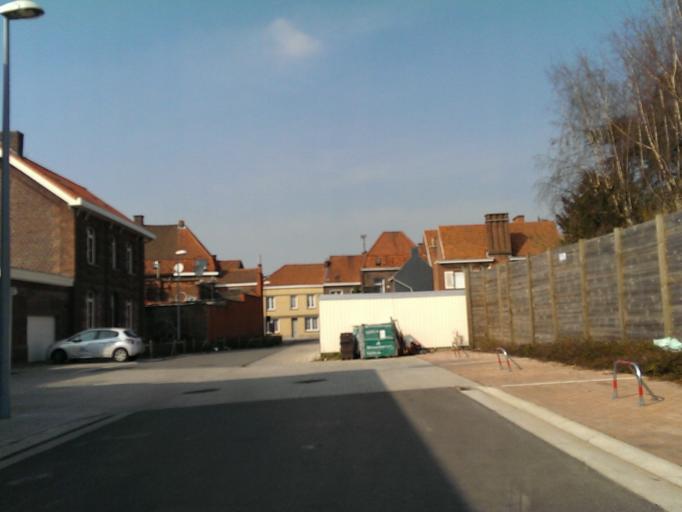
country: BE
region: Flanders
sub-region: Provincie West-Vlaanderen
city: Roeselare
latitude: 50.9498
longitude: 3.1351
